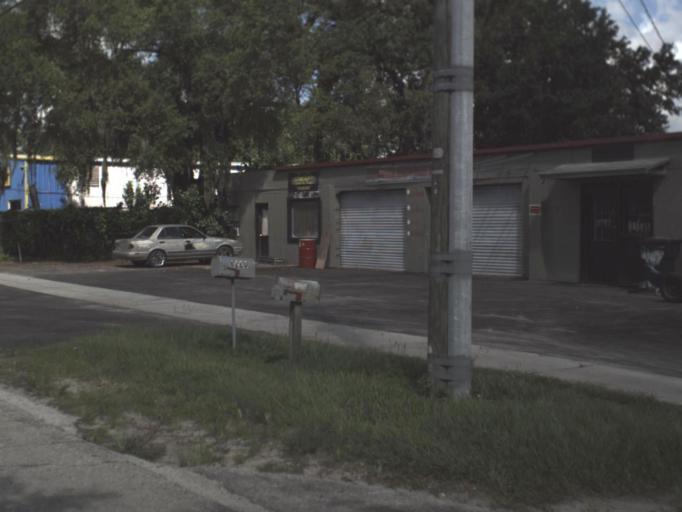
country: US
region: Florida
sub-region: Hillsborough County
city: East Lake-Orient Park
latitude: 27.9663
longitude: -82.3838
